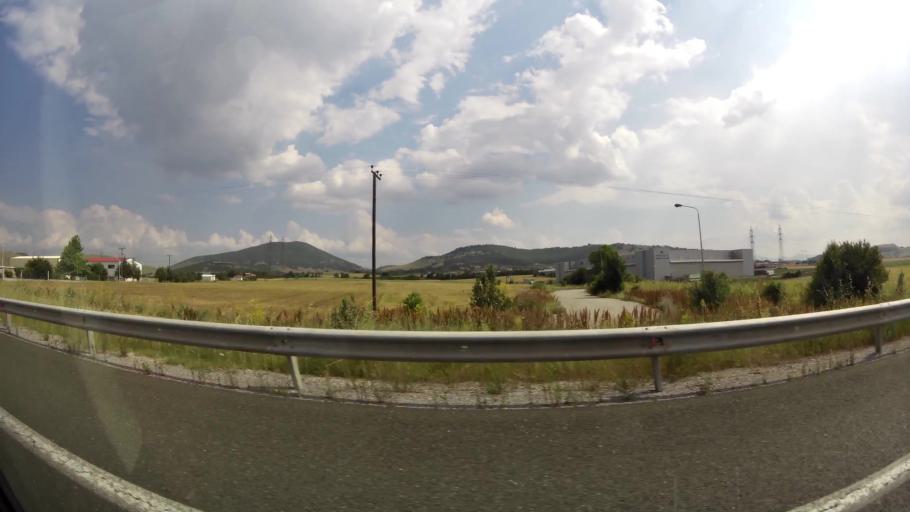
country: GR
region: West Macedonia
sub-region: Nomos Kozanis
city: Koila
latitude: 40.3610
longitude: 21.8435
